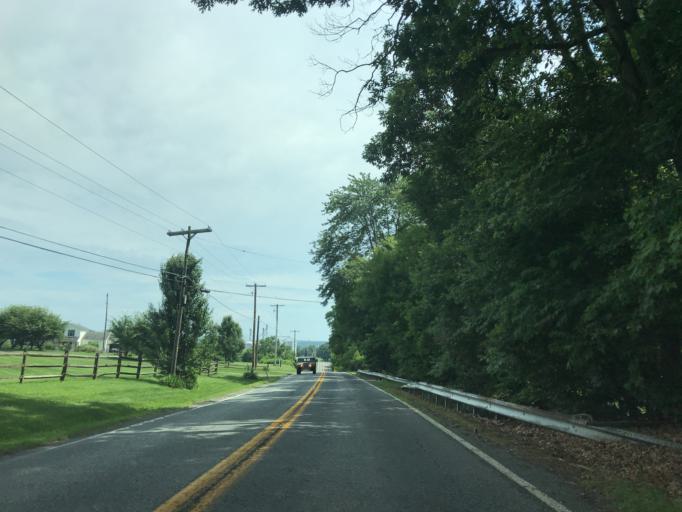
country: US
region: Pennsylvania
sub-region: York County
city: Susquehanna Trails
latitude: 39.7082
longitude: -76.3904
